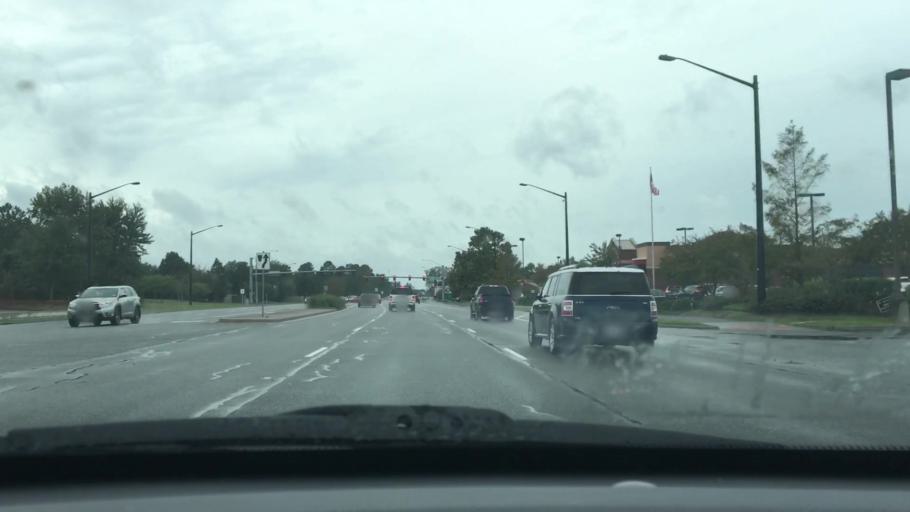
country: US
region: Virginia
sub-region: City of Virginia Beach
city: Virginia Beach
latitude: 36.8120
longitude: -76.0703
